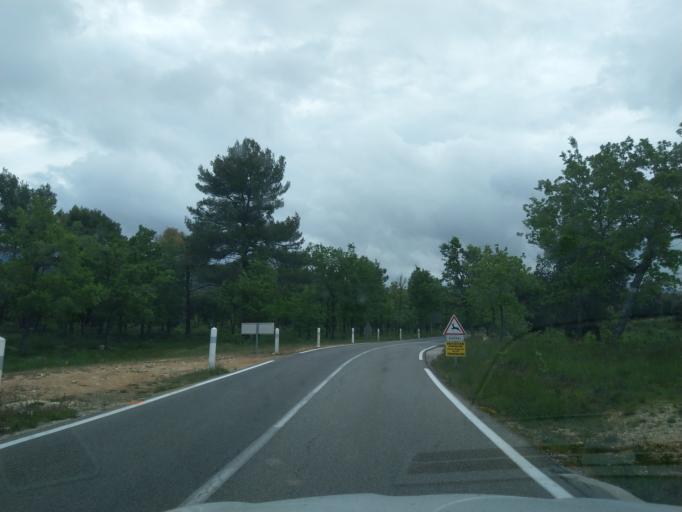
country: FR
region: Provence-Alpes-Cote d'Azur
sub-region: Departement du Var
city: Signes
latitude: 43.2756
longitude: 5.8047
